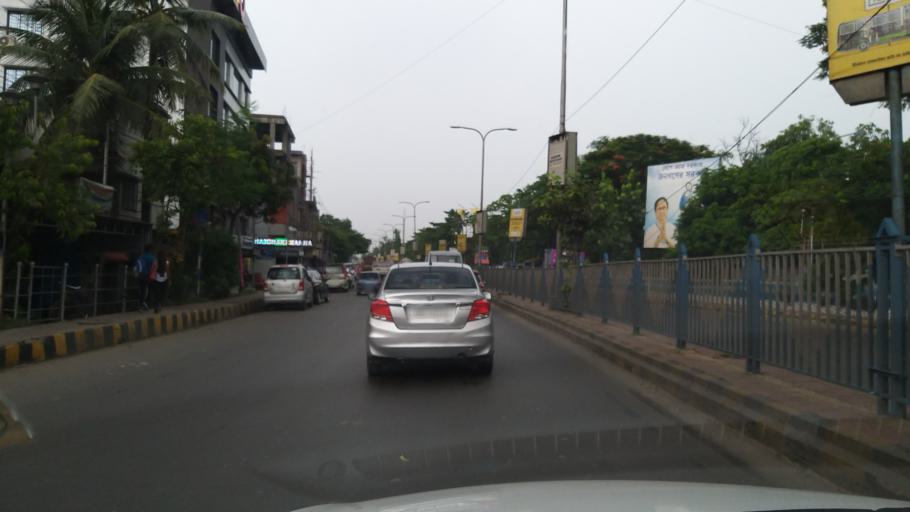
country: IN
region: West Bengal
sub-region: North 24 Parganas
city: Dam Dam
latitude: 22.6562
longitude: 88.4403
